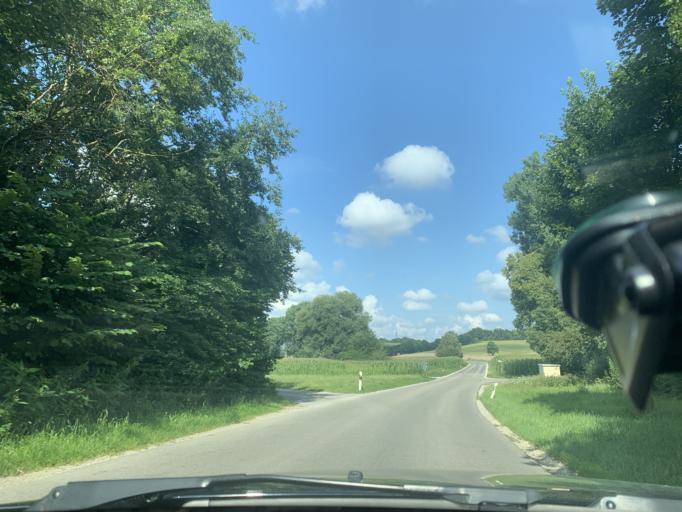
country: DE
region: Bavaria
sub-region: Swabia
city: Mering
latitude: 48.2881
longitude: 11.0144
